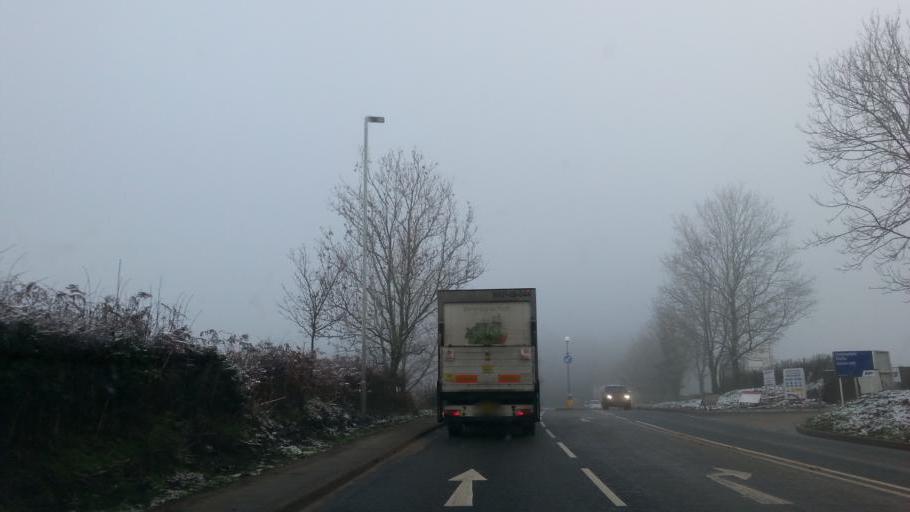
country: GB
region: England
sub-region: Cheshire East
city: Eaton
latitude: 53.1807
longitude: -2.2109
